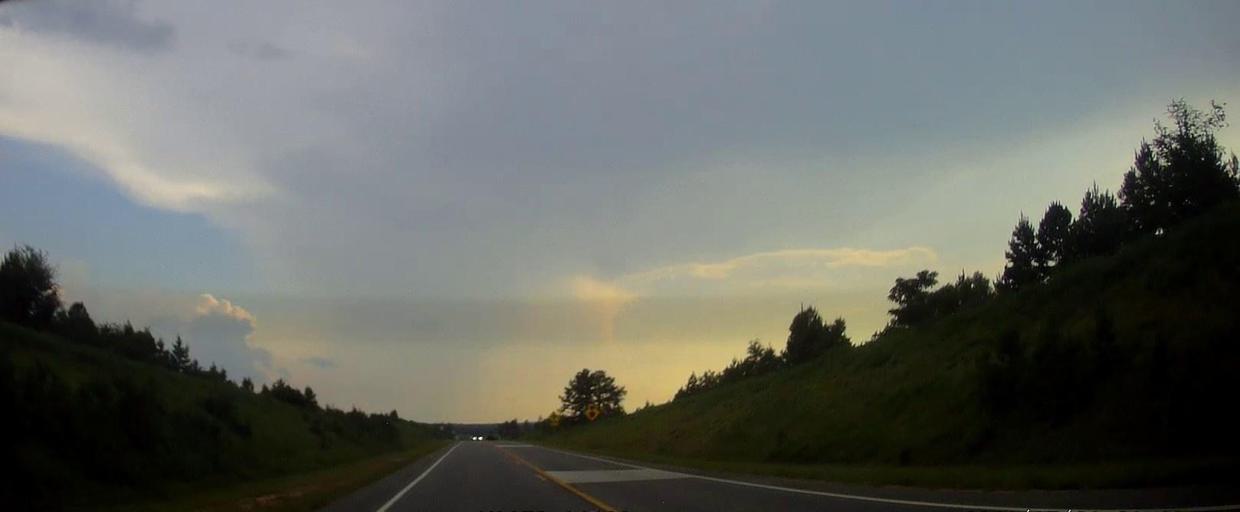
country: US
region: Georgia
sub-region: Laurens County
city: East Dublin
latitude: 32.6238
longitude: -82.8765
